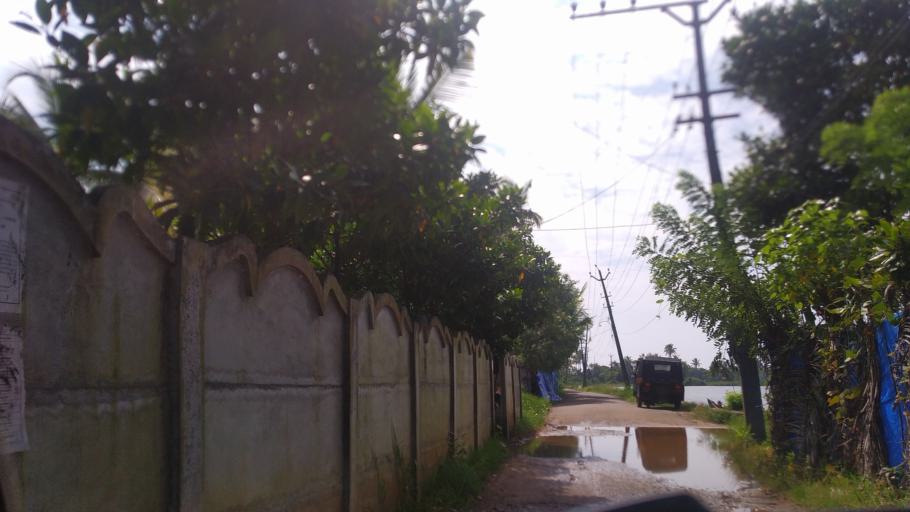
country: IN
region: Kerala
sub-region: Ernakulam
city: Elur
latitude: 10.0828
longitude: 76.2001
